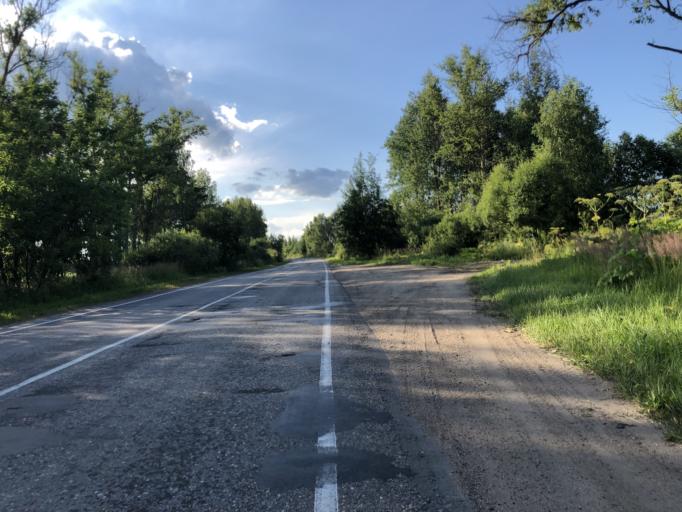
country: RU
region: Tverskaya
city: Rzhev
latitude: 56.2715
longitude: 34.2461
